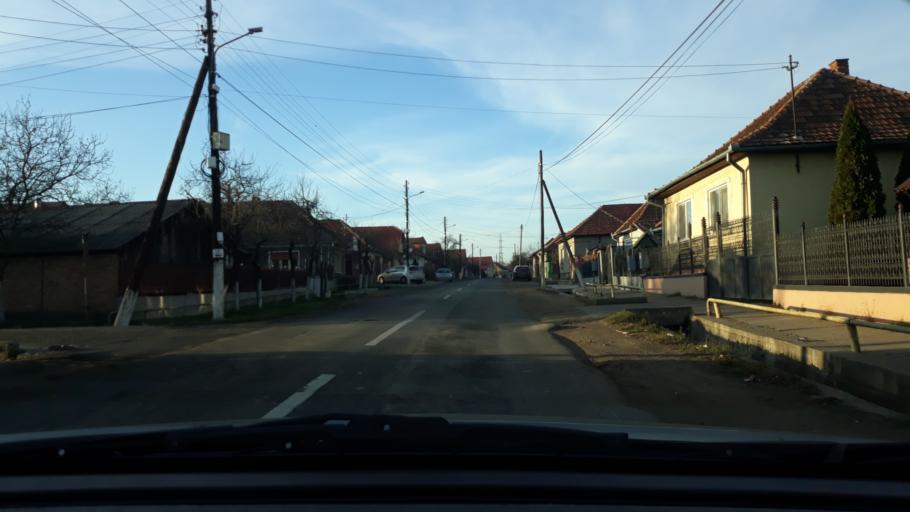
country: RO
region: Bihor
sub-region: Comuna Suplacu de Barcau
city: Suplacu de Barcau
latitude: 47.2594
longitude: 22.5218
